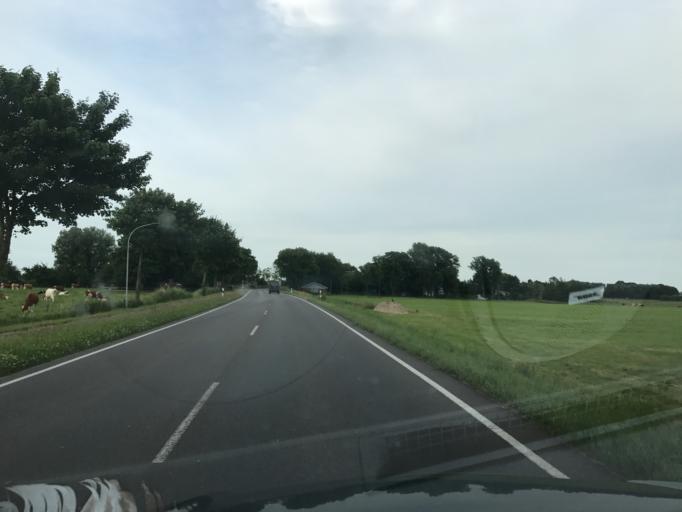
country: DE
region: Schleswig-Holstein
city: Wilster
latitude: 53.9250
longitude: 9.3936
